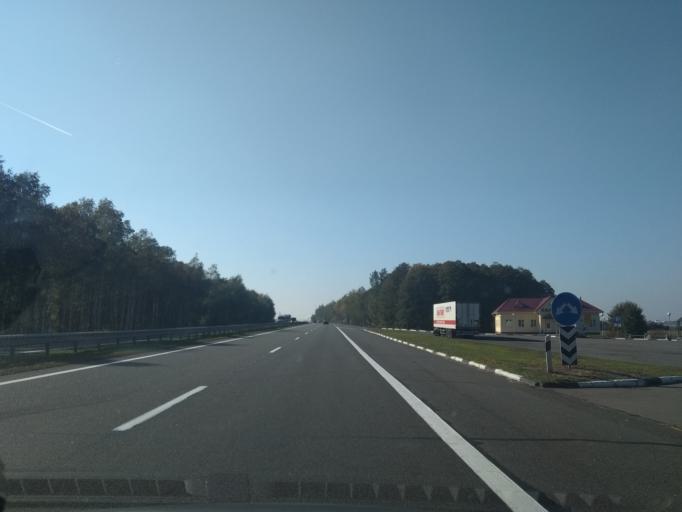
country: BY
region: Brest
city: Ivatsevichy
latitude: 52.7119
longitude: 25.3934
